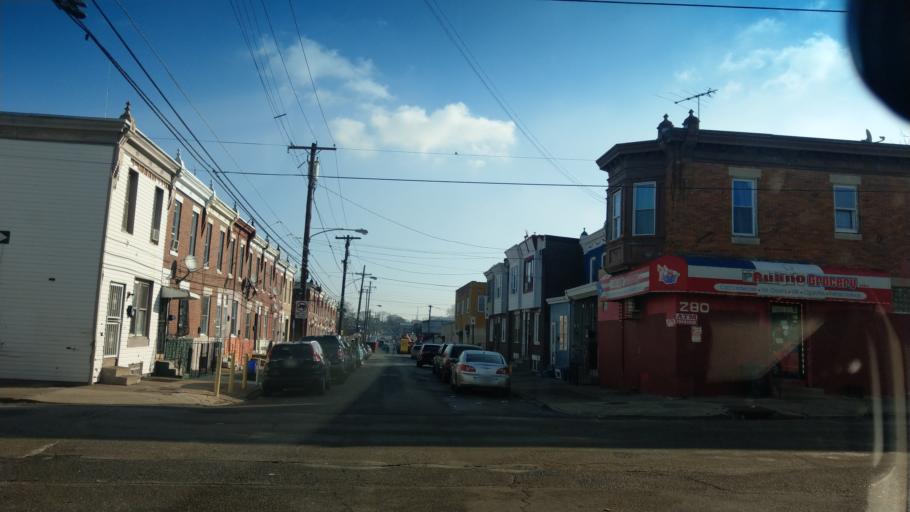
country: US
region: Pennsylvania
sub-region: Philadelphia County
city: Philadelphia
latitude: 40.0193
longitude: -75.1315
